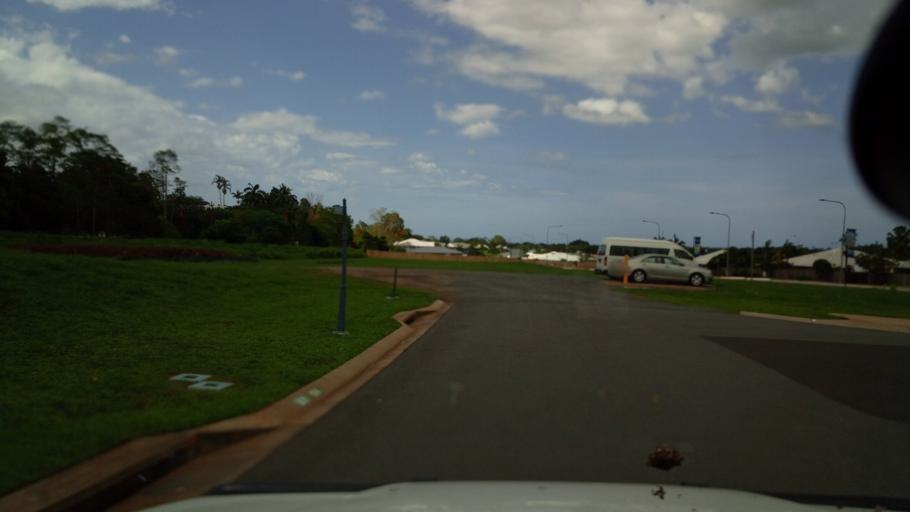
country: AU
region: Queensland
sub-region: Cairns
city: Redlynch
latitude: -16.8959
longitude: 145.6938
